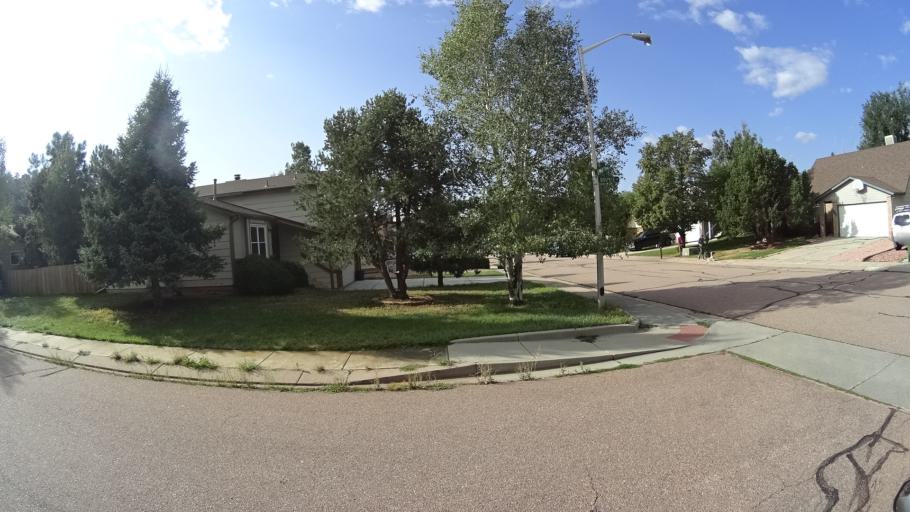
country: US
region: Colorado
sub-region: El Paso County
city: Air Force Academy
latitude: 38.9172
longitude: -104.8607
